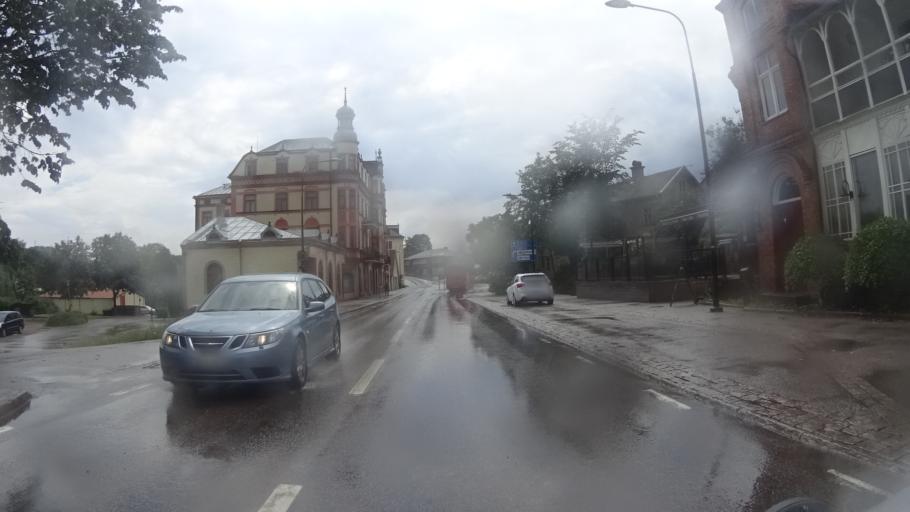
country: SE
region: OEstergoetland
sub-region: Kinda Kommun
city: Kisa
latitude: 57.9901
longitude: 15.6347
